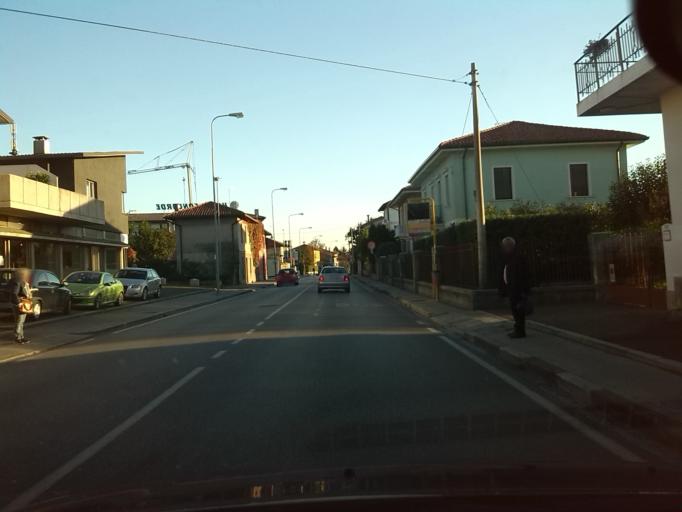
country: IT
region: Friuli Venezia Giulia
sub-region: Provincia di Udine
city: Basaldella
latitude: 46.0444
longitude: 13.2207
